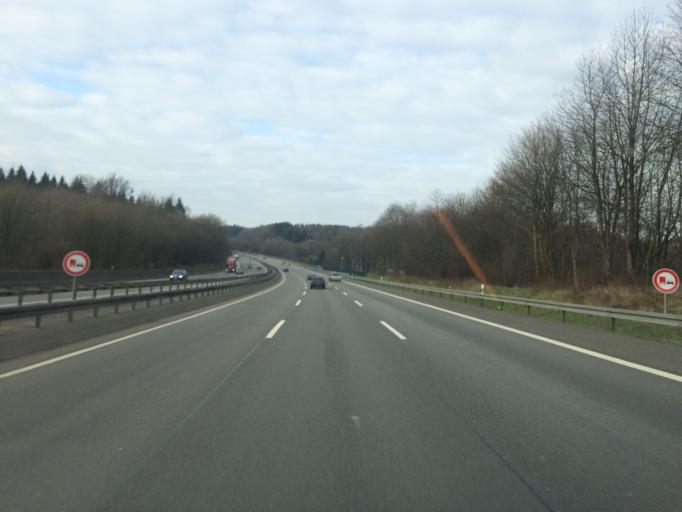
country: DE
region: North Rhine-Westphalia
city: Burscheid
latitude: 51.1198
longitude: 7.1579
